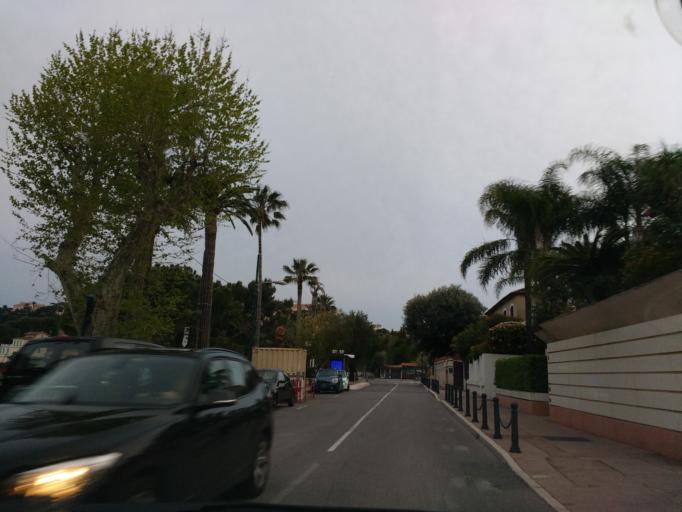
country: FR
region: Provence-Alpes-Cote d'Azur
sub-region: Departement des Alpes-Maritimes
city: Beaulieu-sur-Mer
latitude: 43.7036
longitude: 7.3306
